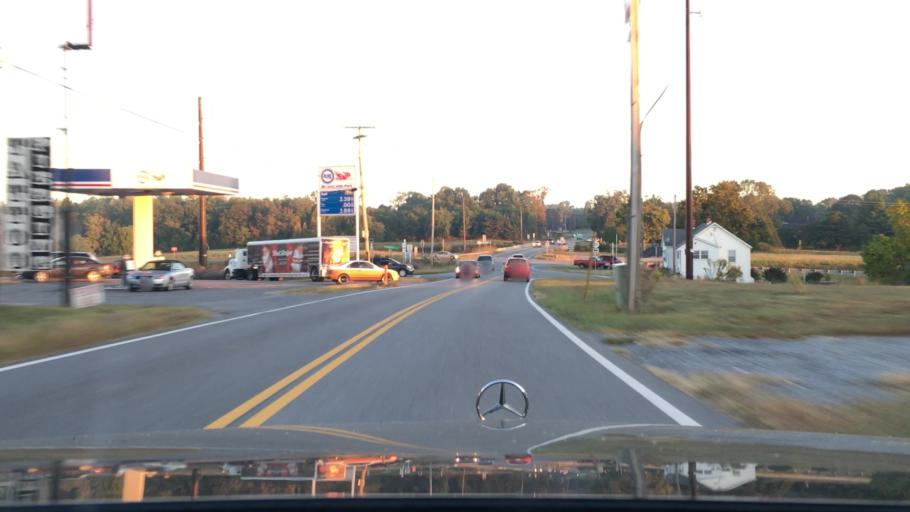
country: US
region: Virginia
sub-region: Campbell County
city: Timberlake
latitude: 37.3103
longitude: -79.2373
